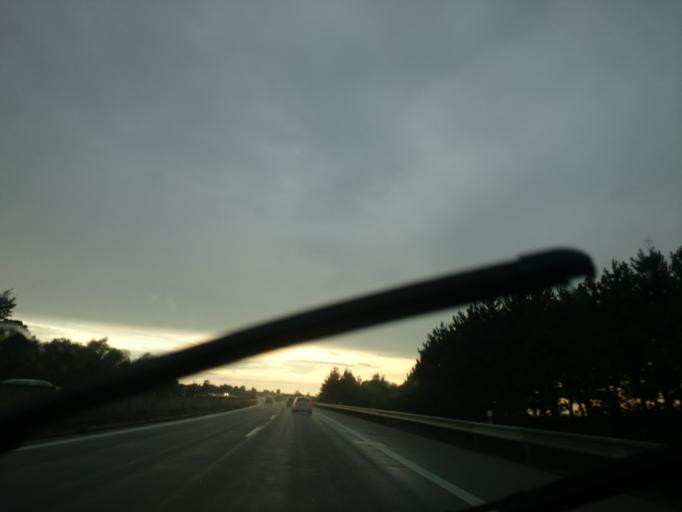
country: CZ
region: Olomoucky
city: Doloplazy
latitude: 49.5856
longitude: 17.4231
